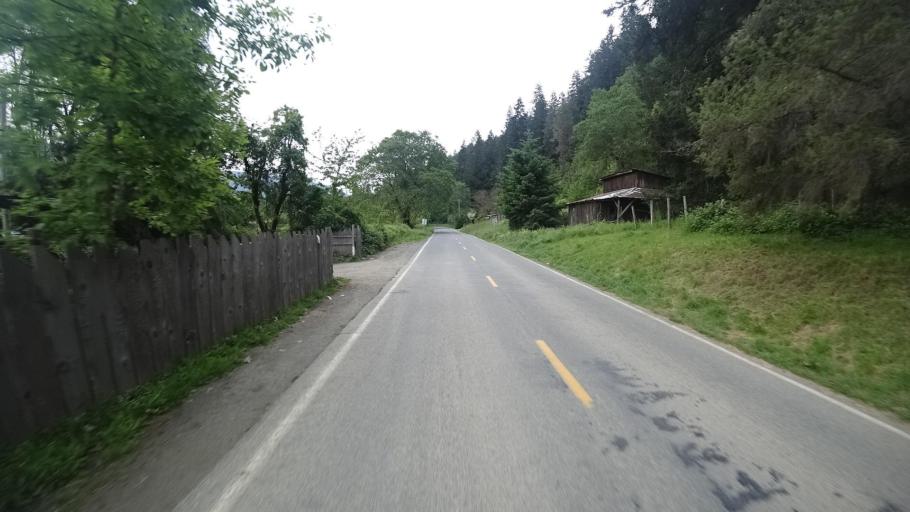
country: US
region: California
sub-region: Humboldt County
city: Willow Creek
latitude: 41.0885
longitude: -123.7119
